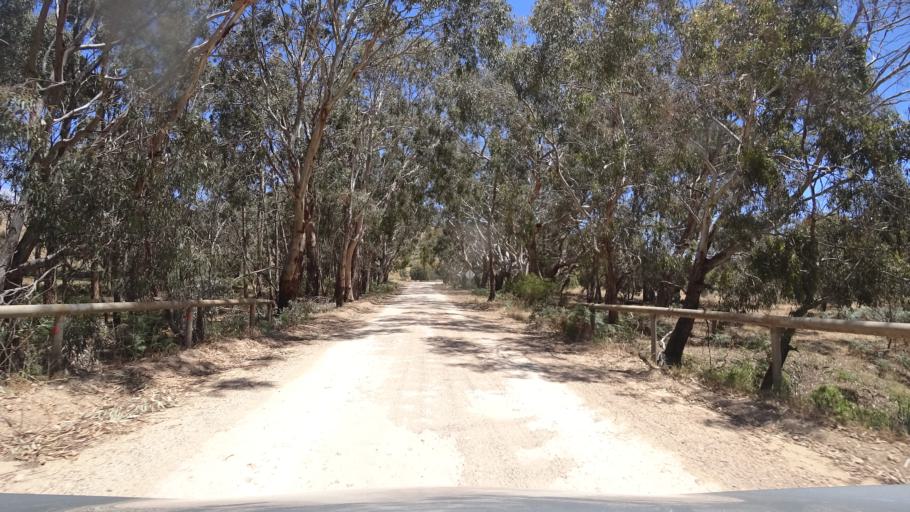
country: AU
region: South Australia
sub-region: Kangaroo Island
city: Kingscote
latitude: -35.6716
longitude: 137.0894
